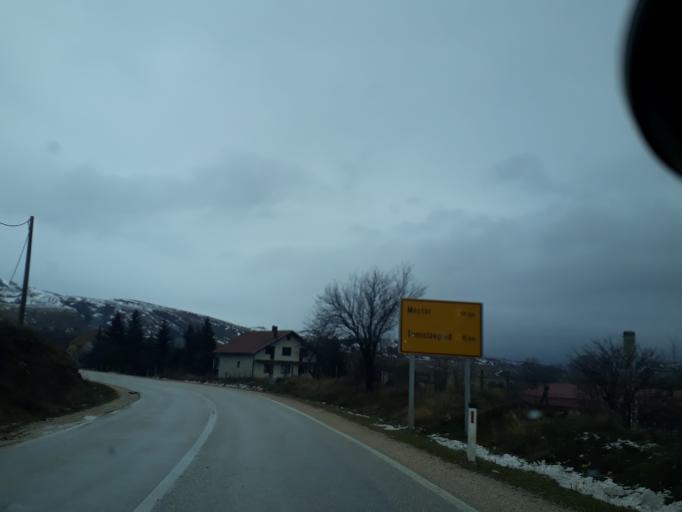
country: BA
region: Federation of Bosnia and Herzegovina
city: Tomislavgrad
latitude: 43.8385
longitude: 17.1791
